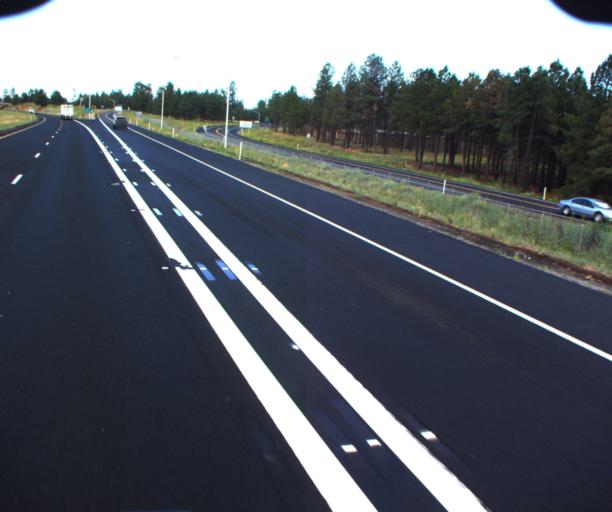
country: US
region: Arizona
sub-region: Coconino County
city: Kachina Village
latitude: 35.1449
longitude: -111.6837
